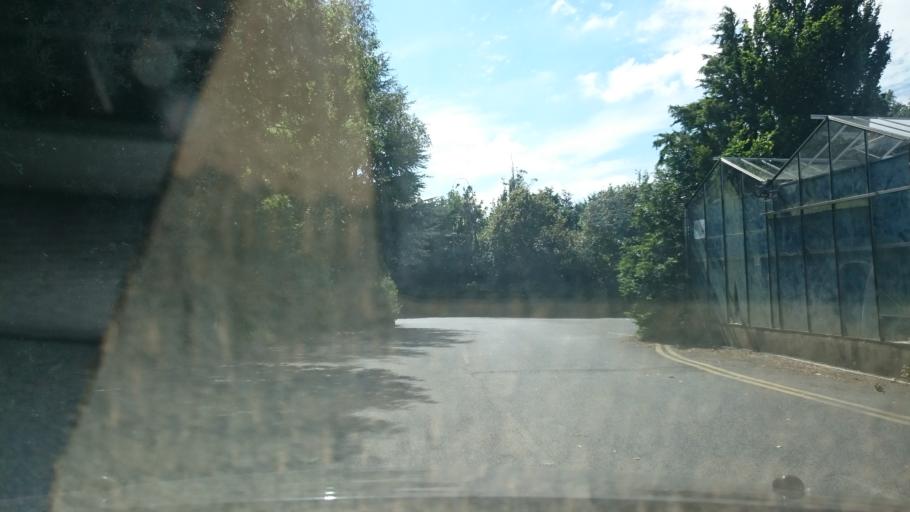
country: IE
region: Leinster
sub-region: Kilkenny
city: Thomastown
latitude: 52.6465
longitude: -7.1152
